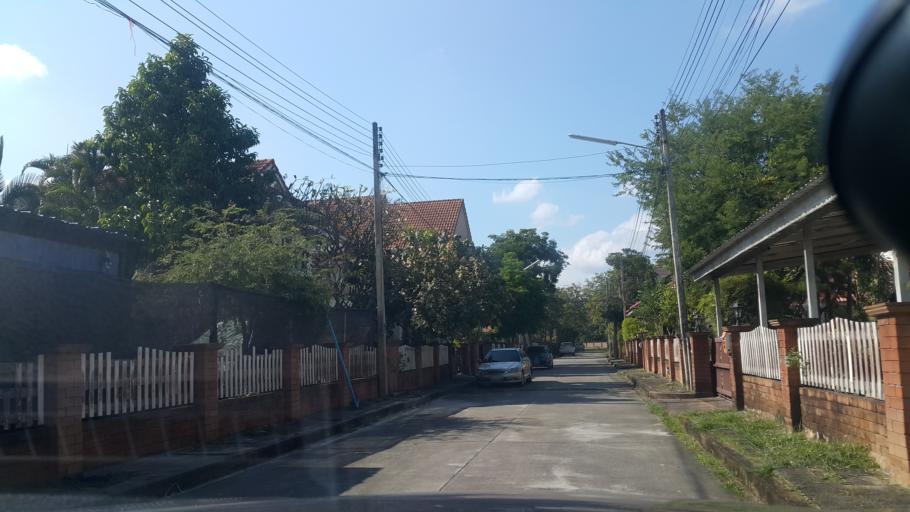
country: TH
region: Chiang Mai
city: Hang Dong
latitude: 18.7299
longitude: 98.9464
